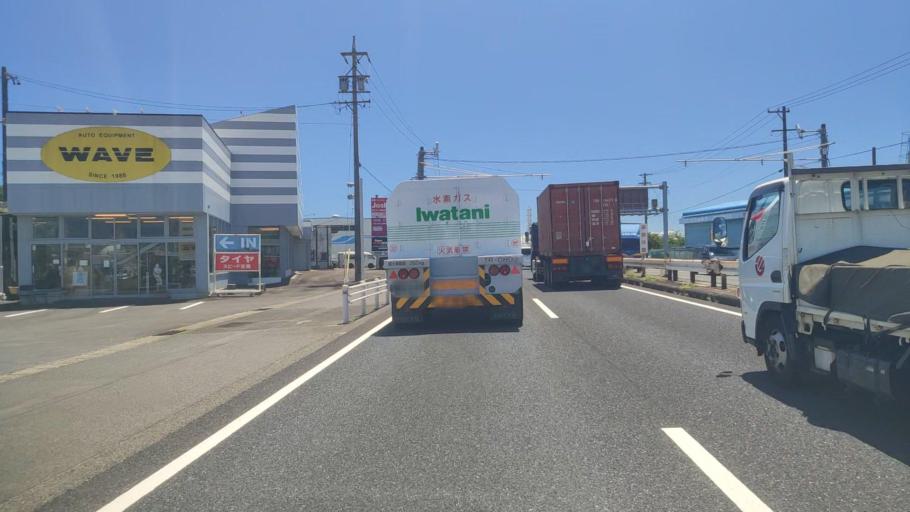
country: JP
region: Mie
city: Yokkaichi
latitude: 34.9434
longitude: 136.6186
